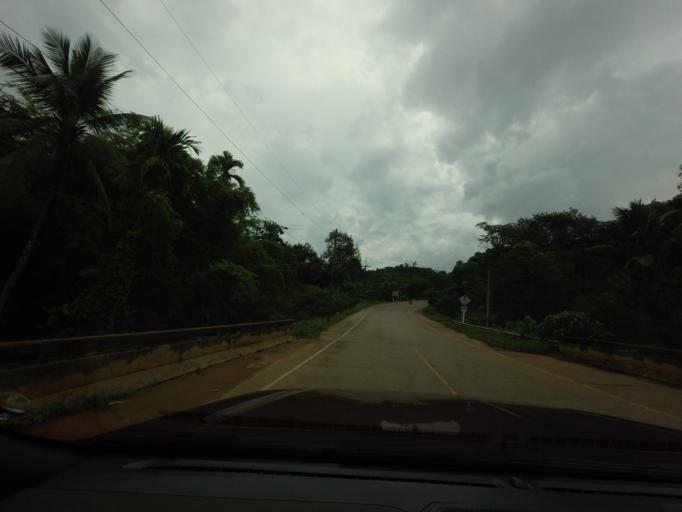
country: TH
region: Narathiwat
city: Sukhirin
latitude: 5.9861
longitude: 101.6841
